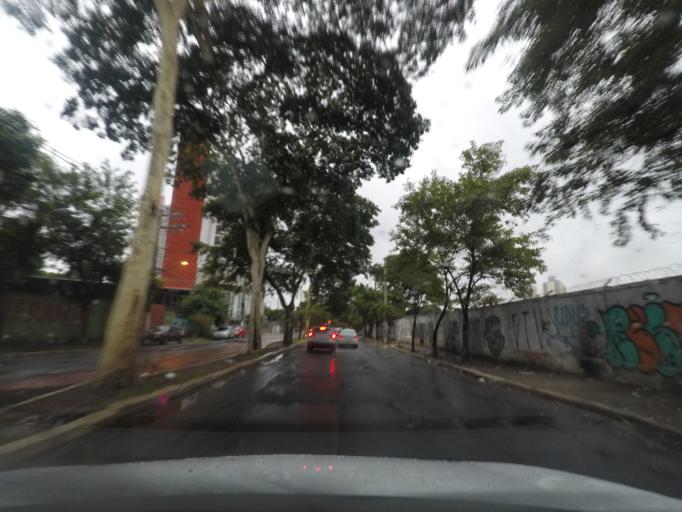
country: BR
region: Sao Paulo
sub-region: Sao Paulo
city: Sao Paulo
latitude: -23.5590
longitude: -46.6279
